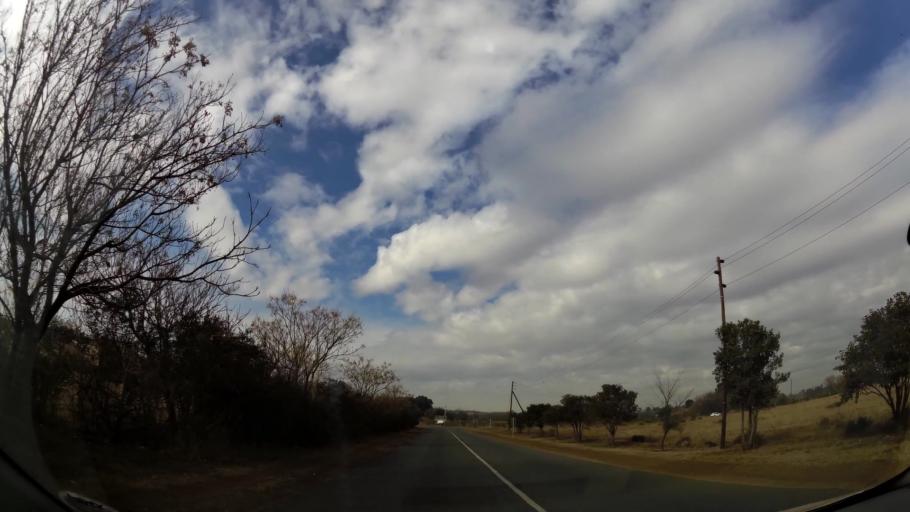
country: ZA
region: Gauteng
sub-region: Sedibeng District Municipality
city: Meyerton
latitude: -26.5564
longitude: 28.0618
